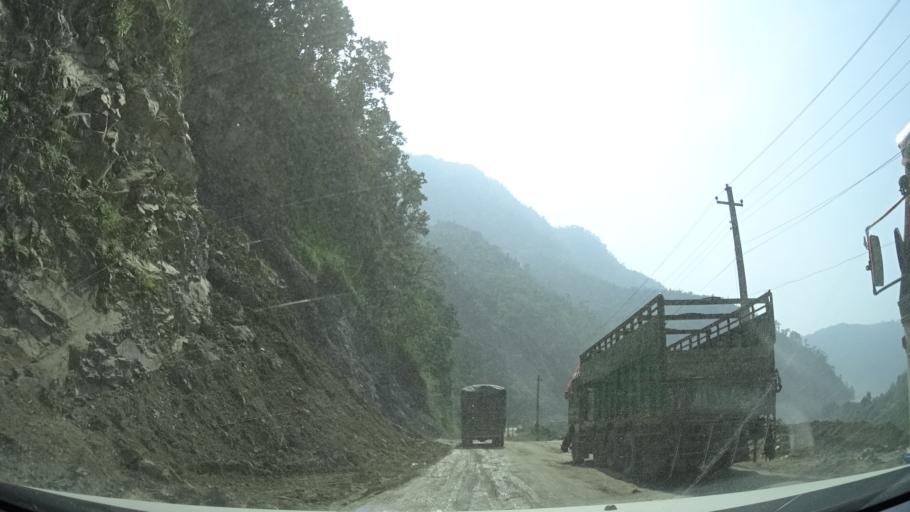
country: NP
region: Central Region
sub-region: Narayani Zone
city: Bharatpur
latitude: 27.8325
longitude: 84.5515
